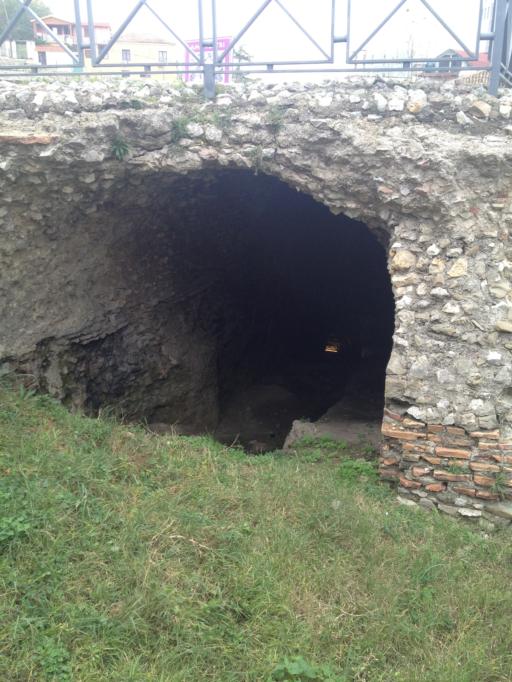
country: AL
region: Durres
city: Durres
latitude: 41.3118
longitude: 19.4447
